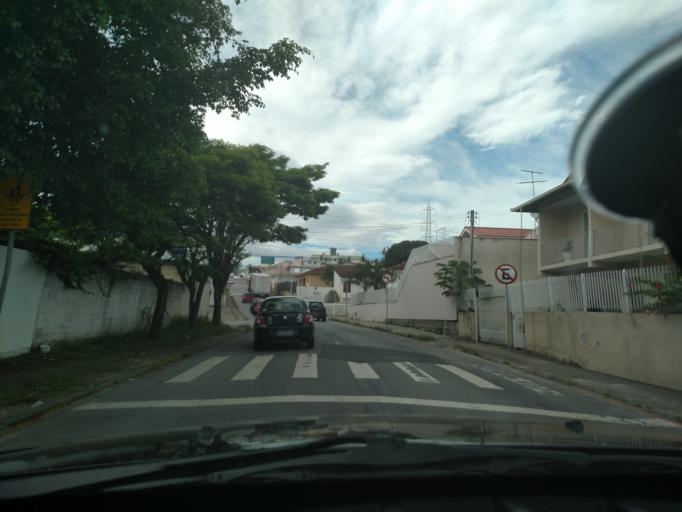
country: BR
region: Santa Catarina
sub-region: Sao Jose
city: Campinas
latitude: -27.6043
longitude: -48.6402
